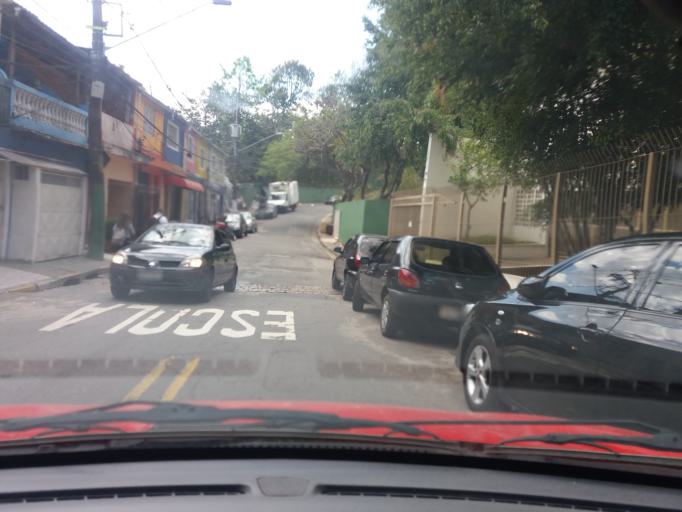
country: BR
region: Sao Paulo
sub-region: Taboao Da Serra
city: Taboao da Serra
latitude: -23.6151
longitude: -46.7470
